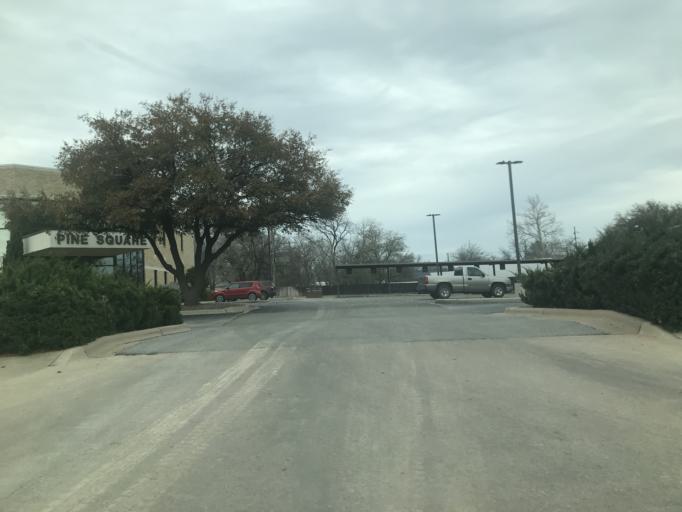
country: US
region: Texas
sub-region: Taylor County
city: Abilene
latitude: 32.4717
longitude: -99.7305
